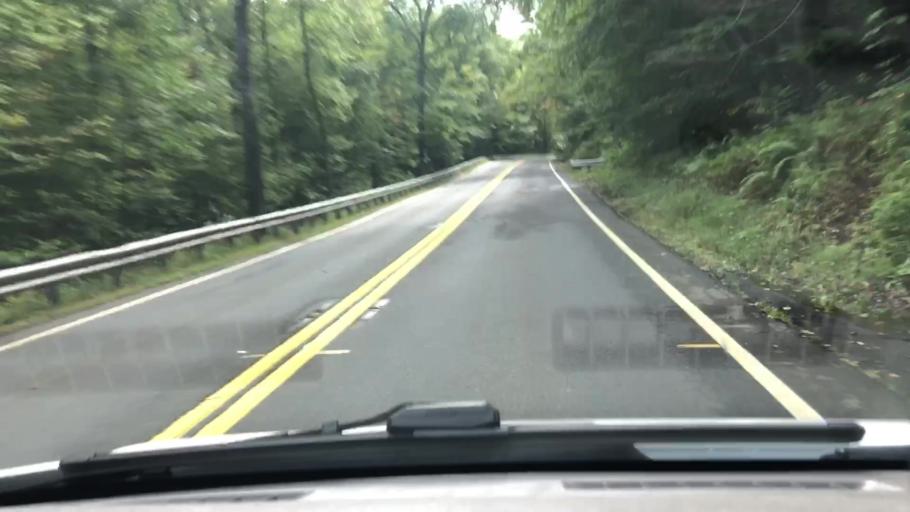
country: US
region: Massachusetts
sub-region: Franklin County
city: Charlemont
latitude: 42.6400
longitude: -72.9404
